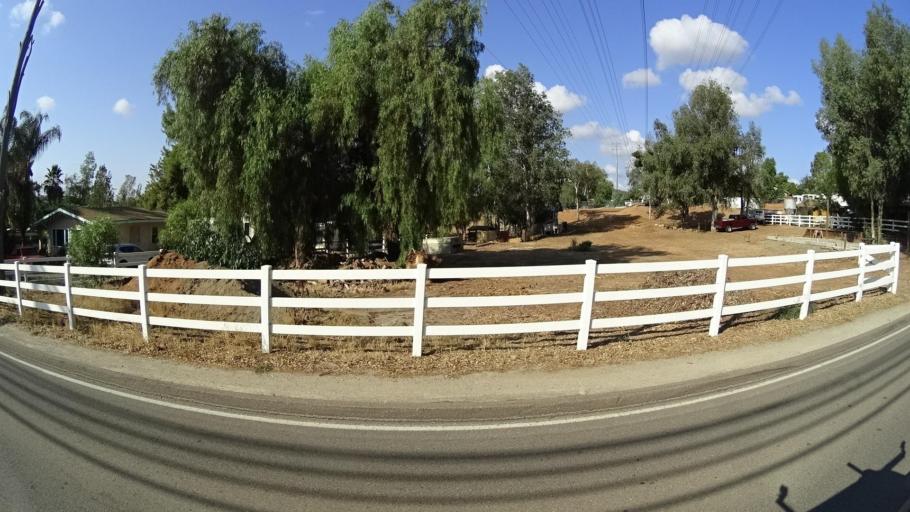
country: US
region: California
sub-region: San Diego County
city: Eucalyptus Hills
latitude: 32.8753
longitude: -116.9362
